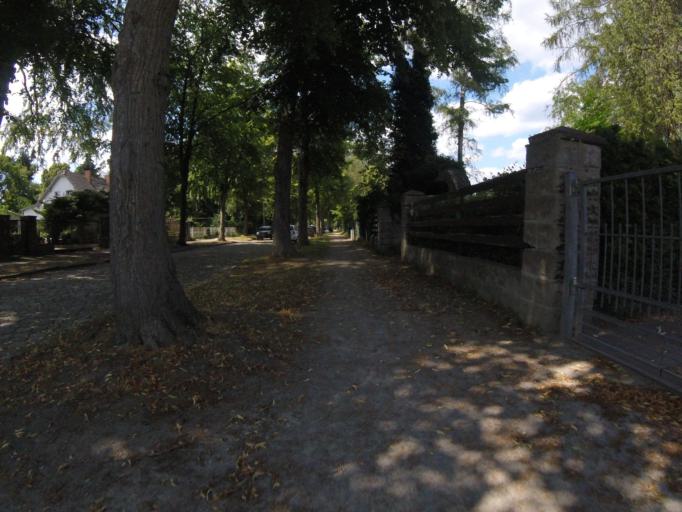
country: DE
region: Brandenburg
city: Wildau
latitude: 52.3372
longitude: 13.6431
